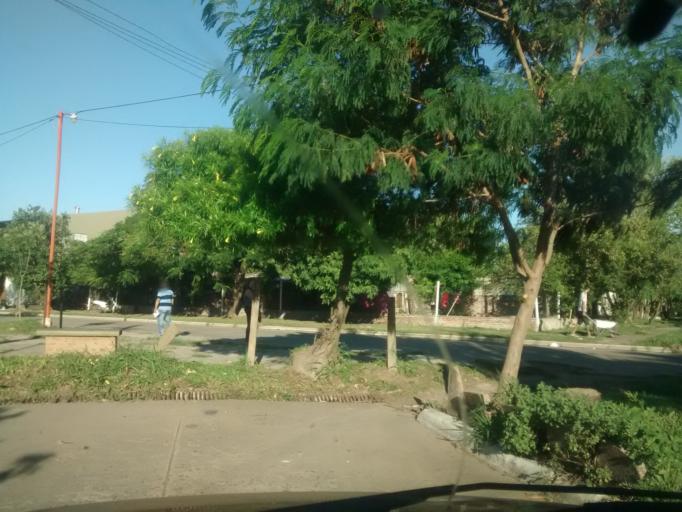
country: AR
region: Chaco
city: Resistencia
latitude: -27.4541
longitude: -59.0131
